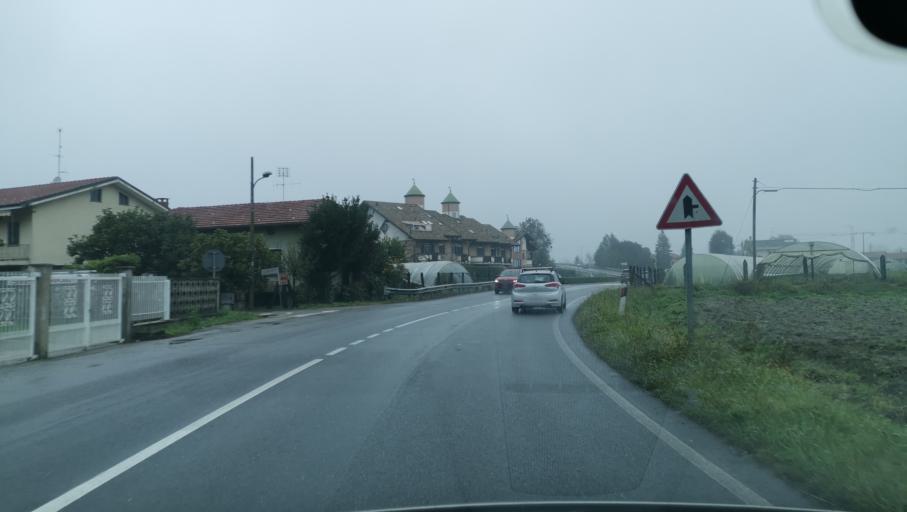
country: IT
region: Piedmont
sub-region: Provincia di Torino
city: Castiglione Torinese
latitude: 45.1205
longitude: 7.7923
